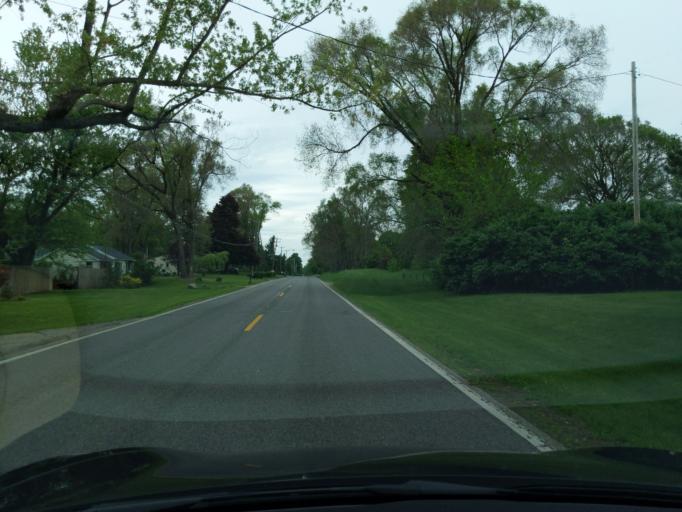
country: US
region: Michigan
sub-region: Ingham County
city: Leslie
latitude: 42.3749
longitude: -84.3491
